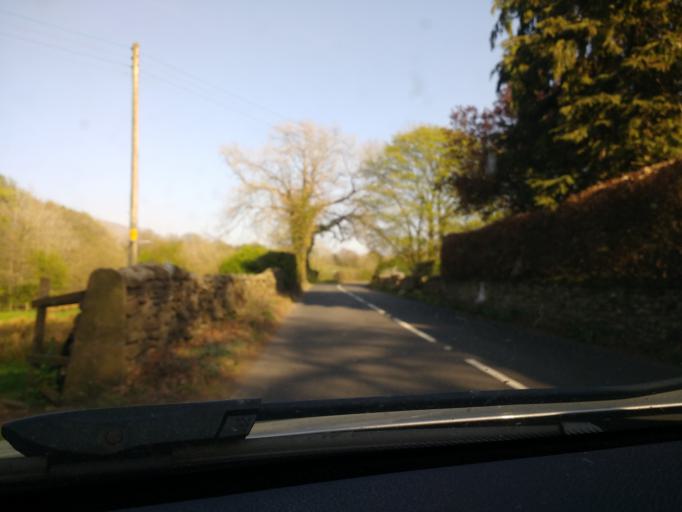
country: GB
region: England
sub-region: Cumbria
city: Sedbergh
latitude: 54.3195
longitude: -2.4912
